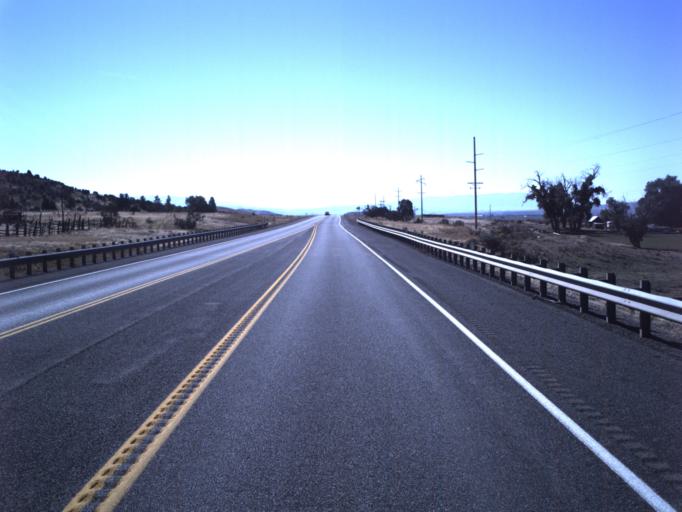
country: US
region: Utah
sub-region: Sanpete County
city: Gunnison
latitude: 39.2280
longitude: -111.8479
